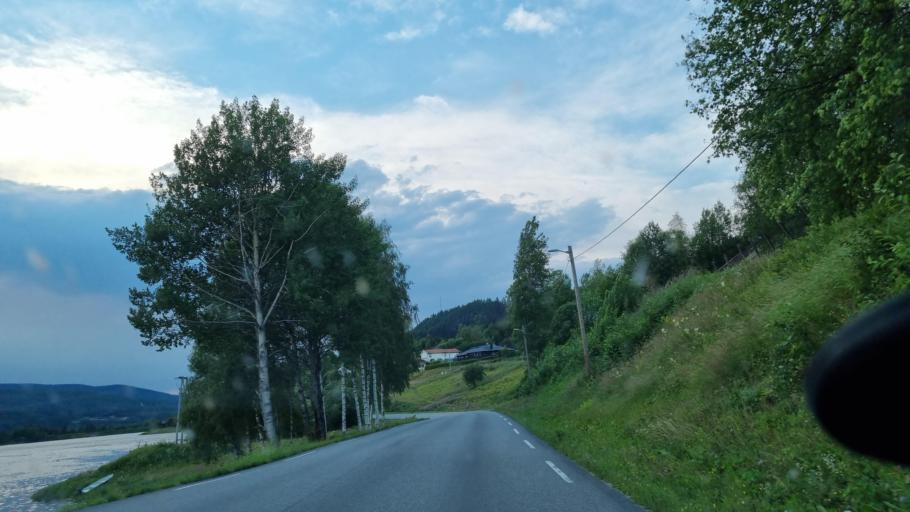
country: NO
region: Hedmark
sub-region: Trysil
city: Innbygda
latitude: 61.3219
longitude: 12.2584
